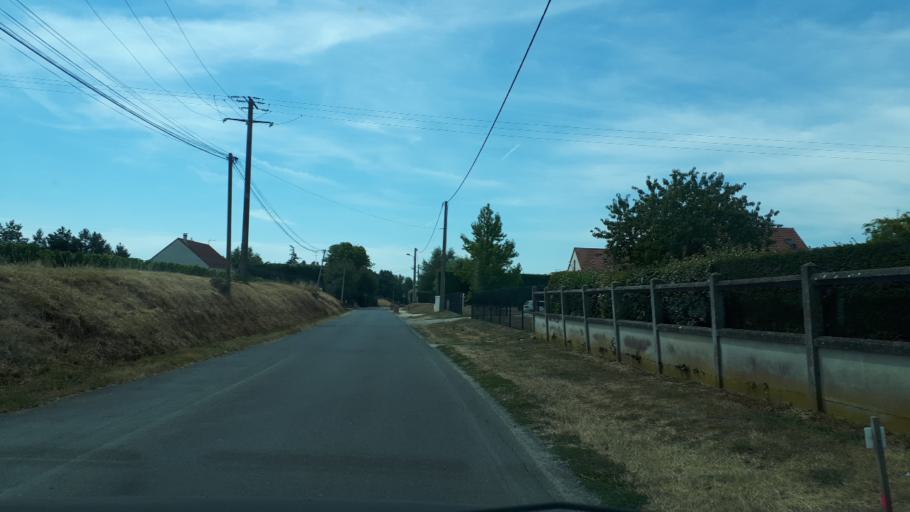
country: FR
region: Centre
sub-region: Departement du Loir-et-Cher
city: Contres
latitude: 47.3950
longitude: 1.3782
